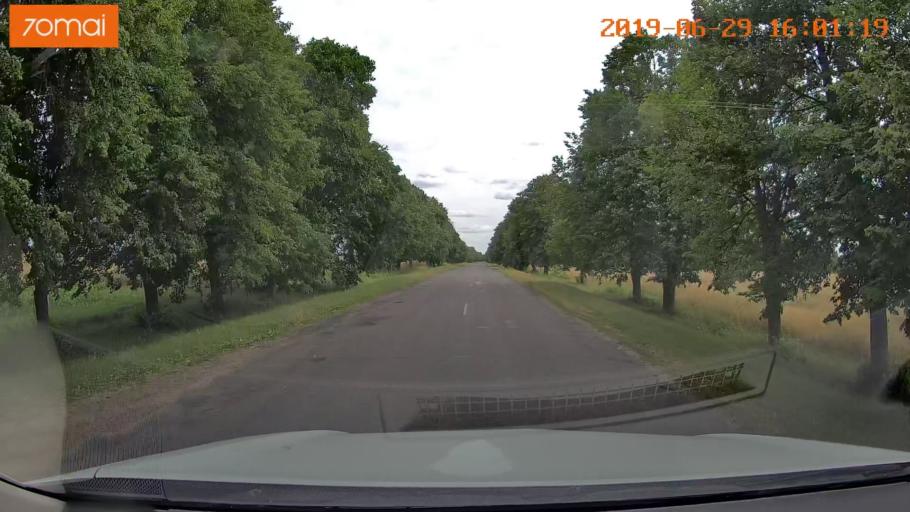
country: BY
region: Brest
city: Luninyets
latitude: 52.2490
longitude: 27.0167
